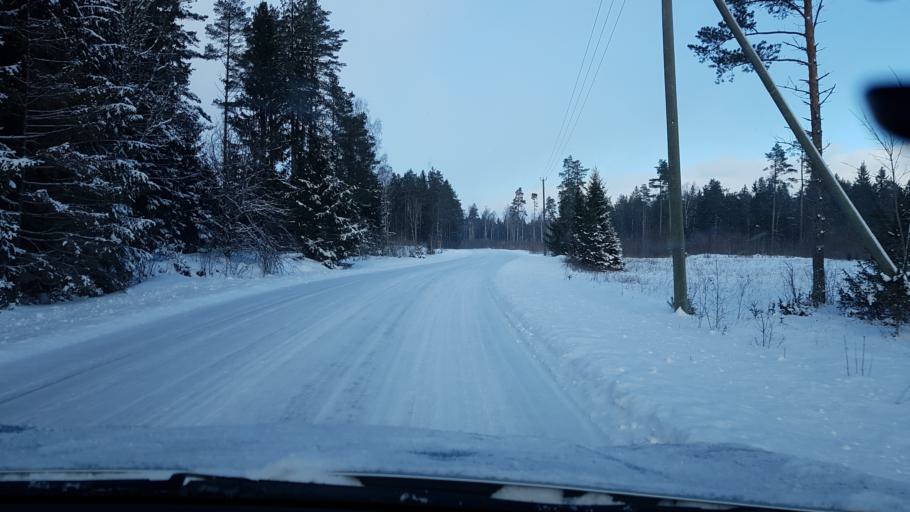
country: EE
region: Harju
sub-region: Nissi vald
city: Turba
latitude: 59.1913
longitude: 24.1397
